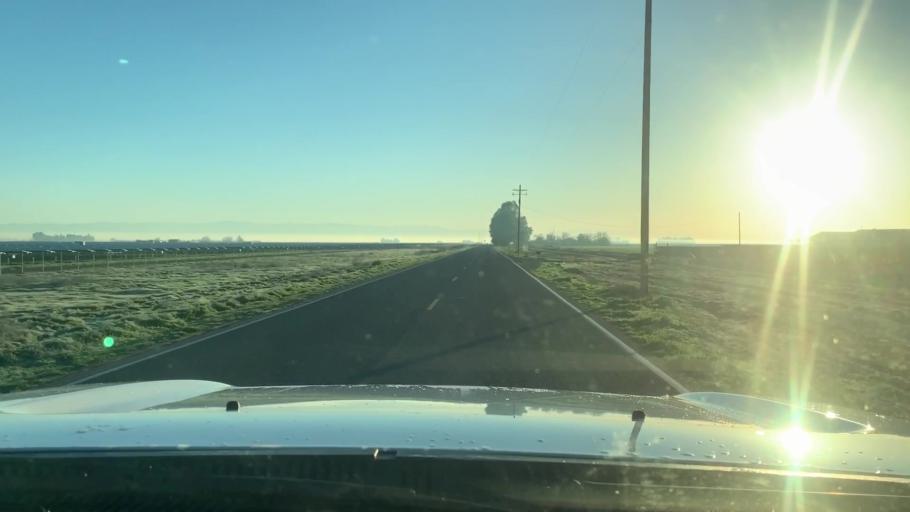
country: US
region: California
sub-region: Kings County
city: Stratford
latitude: 36.2115
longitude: -119.8122
